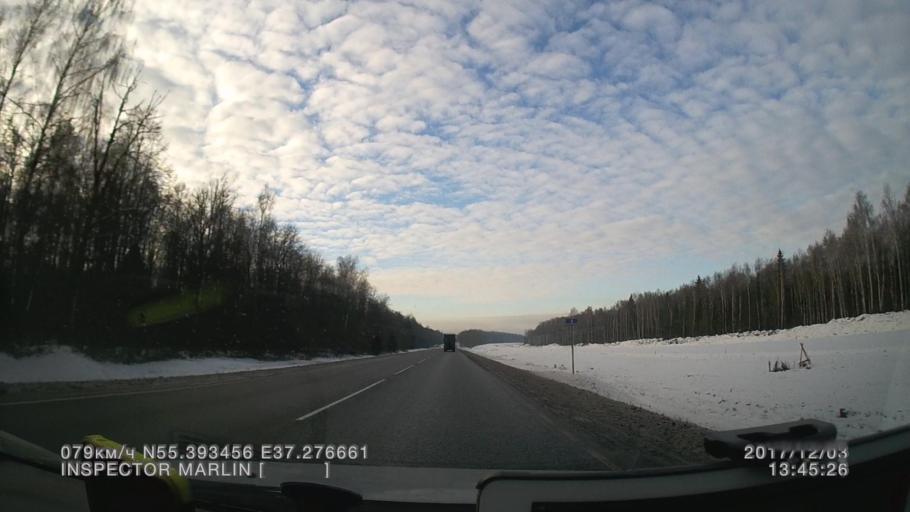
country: RU
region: Moskovskaya
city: Troitsk
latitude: 55.3934
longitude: 37.2771
